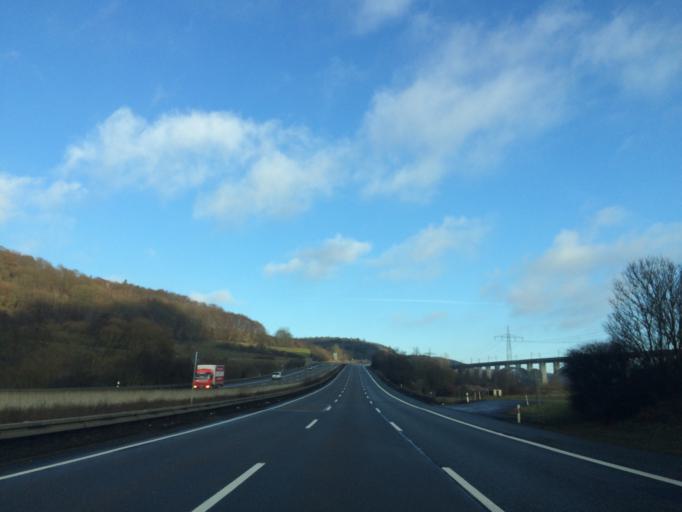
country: DE
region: Hesse
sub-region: Regierungsbezirk Kassel
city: Kirchheim
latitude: 50.8493
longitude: 9.5857
